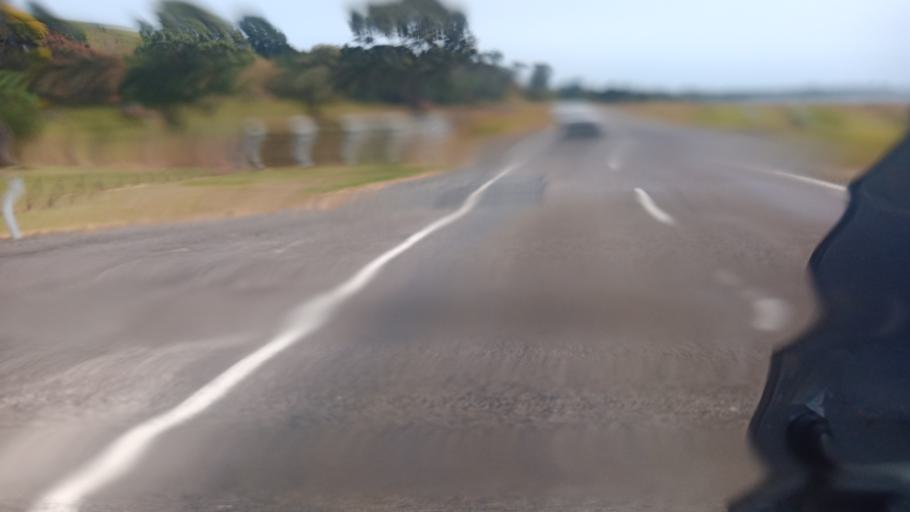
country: NZ
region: Bay of Plenty
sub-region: Opotiki District
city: Opotiki
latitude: -37.6210
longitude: 177.9284
